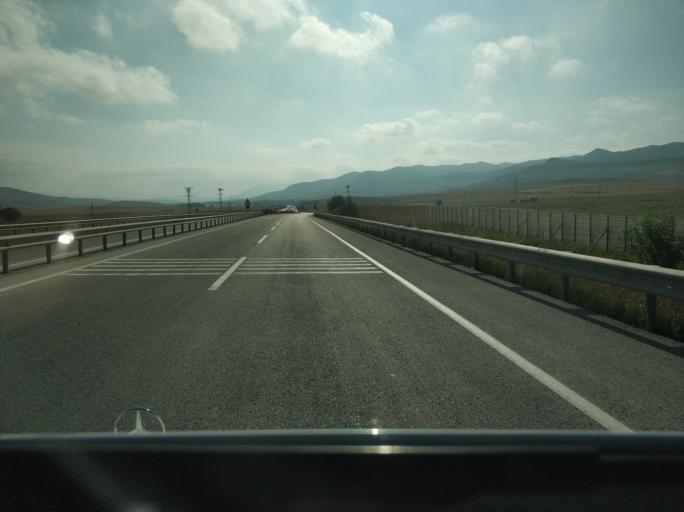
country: TR
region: Sivas
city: Yildizeli
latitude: 39.8349
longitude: 36.4242
